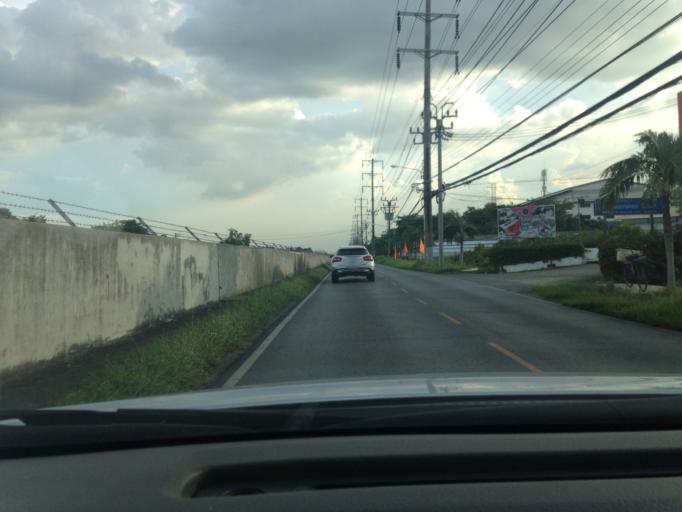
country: TH
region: Bangkok
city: Don Mueang
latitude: 13.9163
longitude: 100.5593
